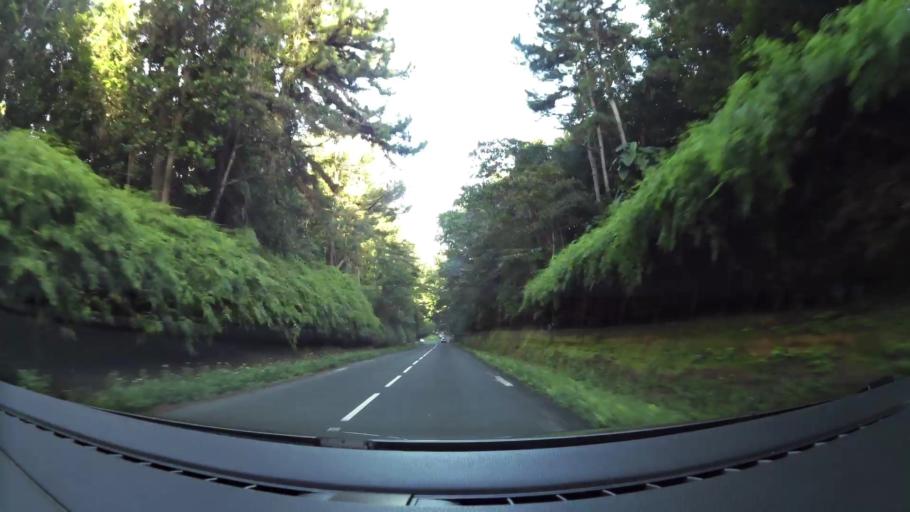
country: GP
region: Guadeloupe
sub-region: Guadeloupe
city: Bouillante
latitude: 16.1751
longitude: -61.6960
